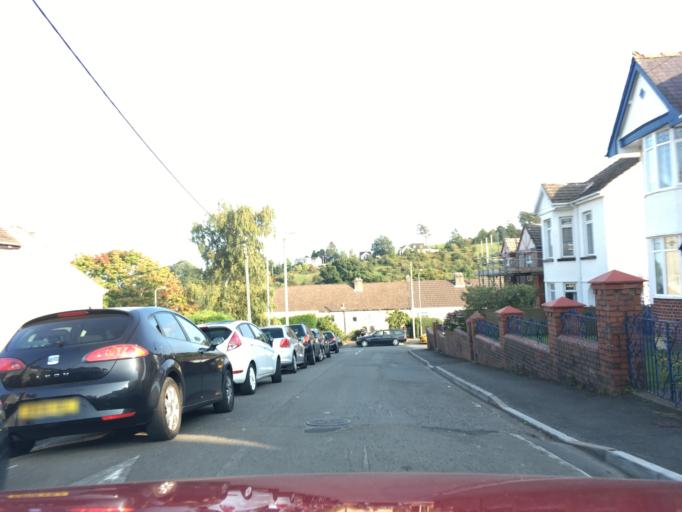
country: GB
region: Wales
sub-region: Torfaen County Borough
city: Pontypool
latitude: 51.6956
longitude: -3.0374
